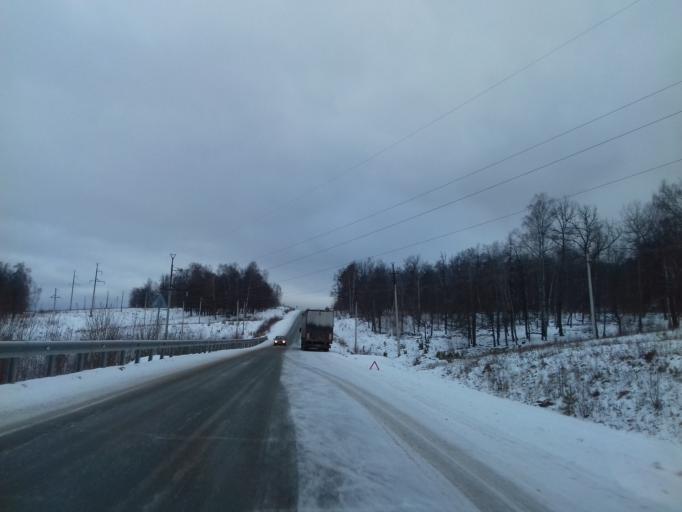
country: RU
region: Bashkortostan
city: Starosubkhangulovo
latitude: 53.2649
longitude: 57.5140
